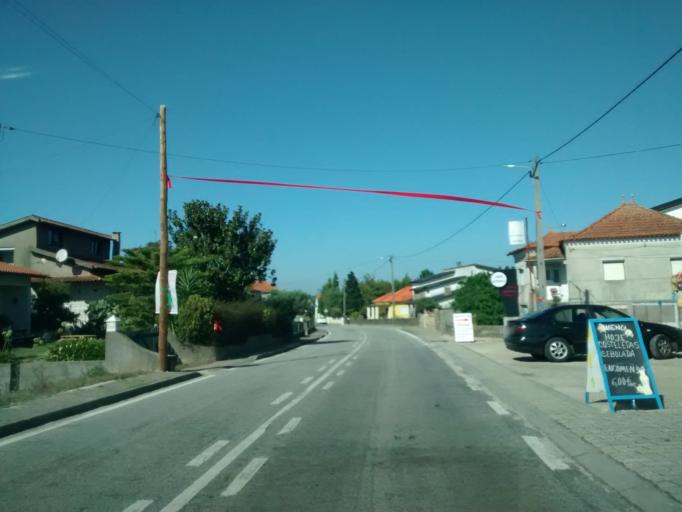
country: PT
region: Aveiro
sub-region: Anadia
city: Sangalhos
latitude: 40.4312
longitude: -8.5121
